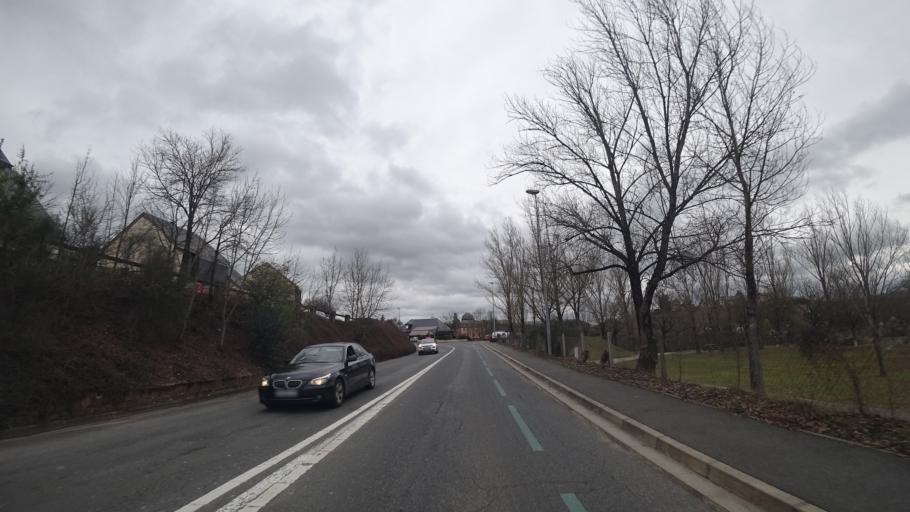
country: FR
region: Midi-Pyrenees
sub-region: Departement de l'Aveyron
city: Rodez
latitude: 44.3632
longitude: 2.5660
